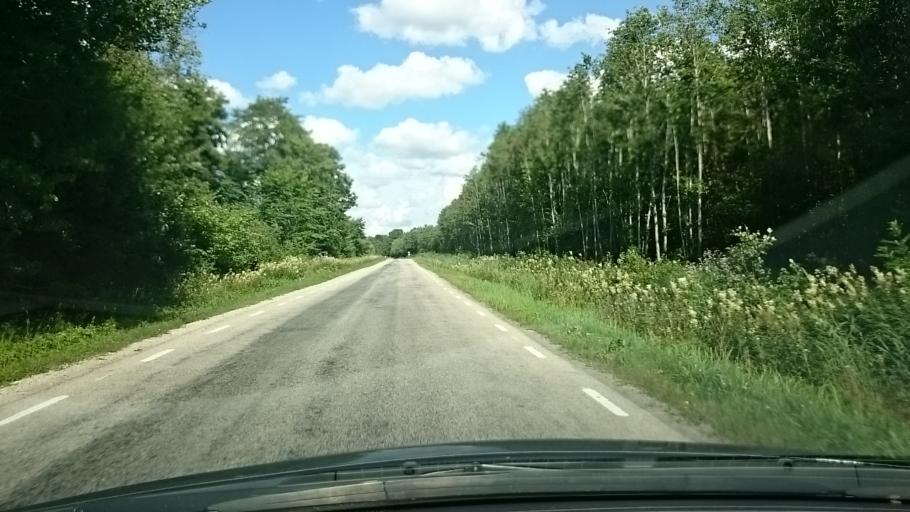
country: EE
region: Laeaene
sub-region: Ridala Parish
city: Uuemoisa
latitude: 59.0654
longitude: 23.5765
